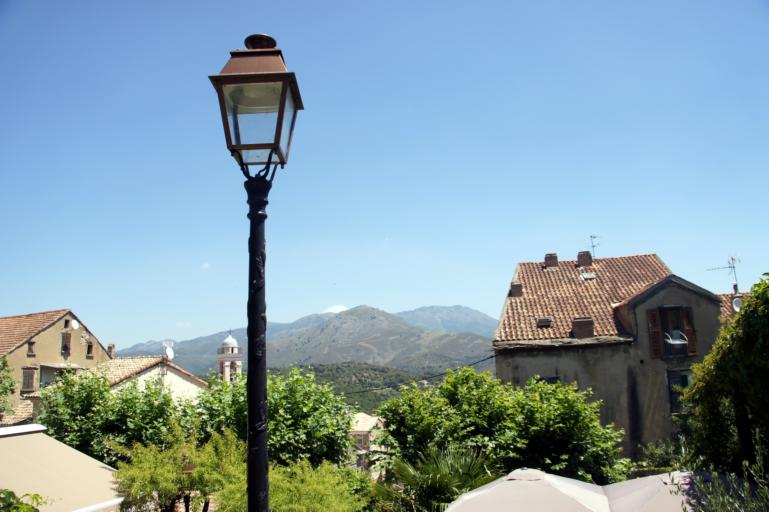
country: FR
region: Corsica
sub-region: Departement de la Haute-Corse
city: Corte
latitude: 42.3051
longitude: 9.1490
